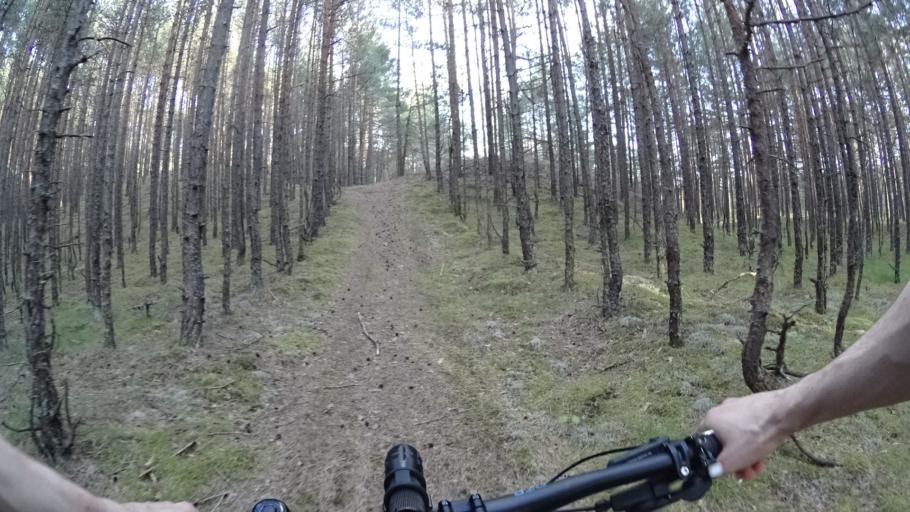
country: LV
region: Riga
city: Jaunciems
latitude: 57.1081
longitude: 24.1894
